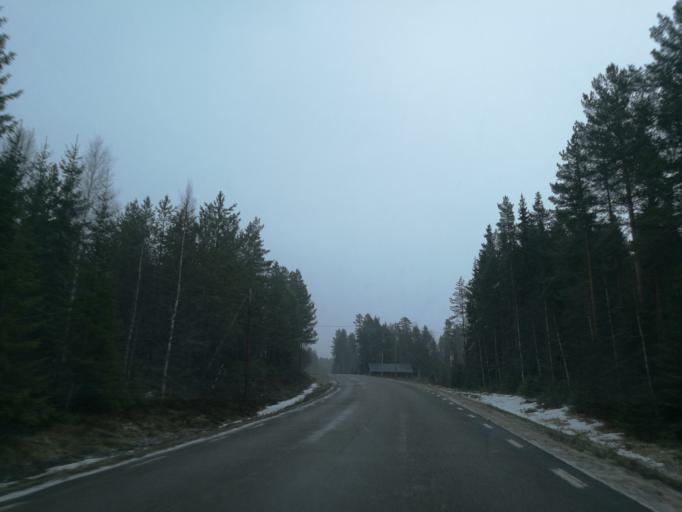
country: NO
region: Hedmark
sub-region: Asnes
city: Flisa
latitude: 60.6965
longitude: 12.4963
